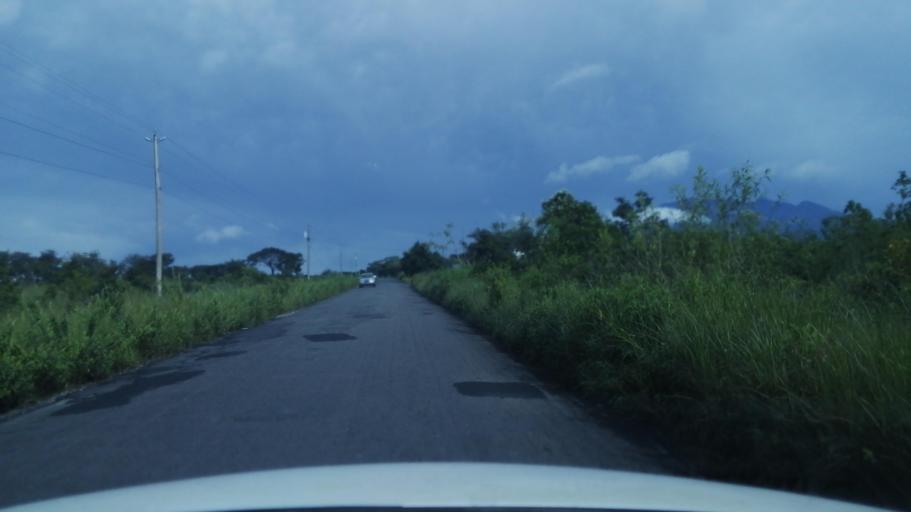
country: PA
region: Chiriqui
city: Potrerillos Abajo
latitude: 8.6696
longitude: -82.4325
